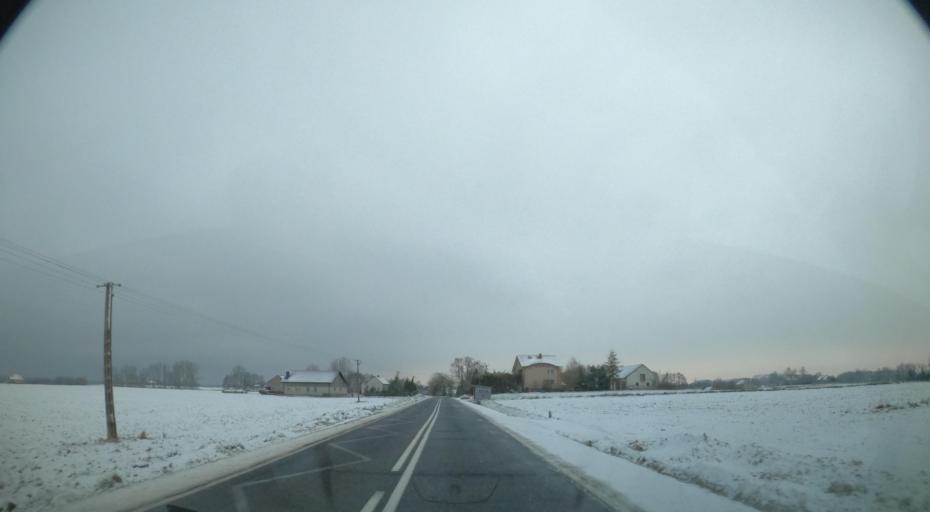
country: PL
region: Masovian Voivodeship
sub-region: Powiat plocki
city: Nowy Duninow
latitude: 52.6286
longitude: 19.4261
